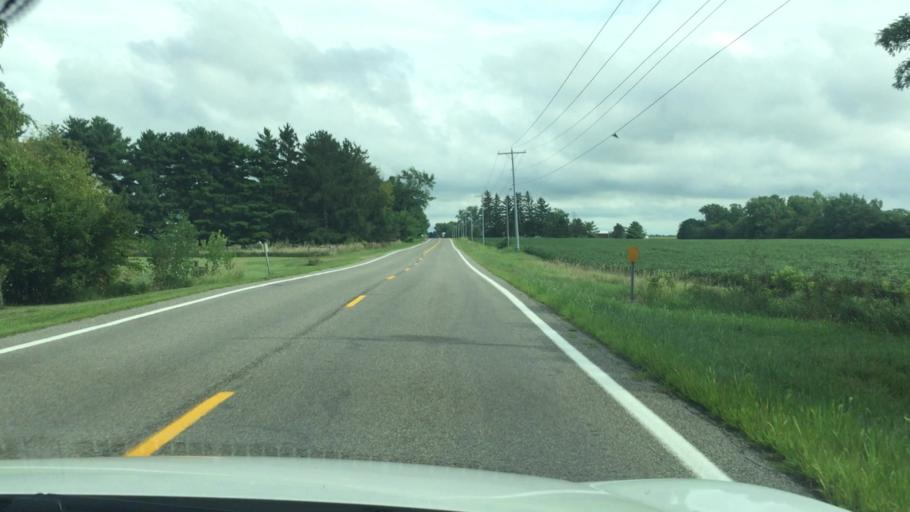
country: US
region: Ohio
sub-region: Champaign County
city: North Lewisburg
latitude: 40.2075
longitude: -83.5388
